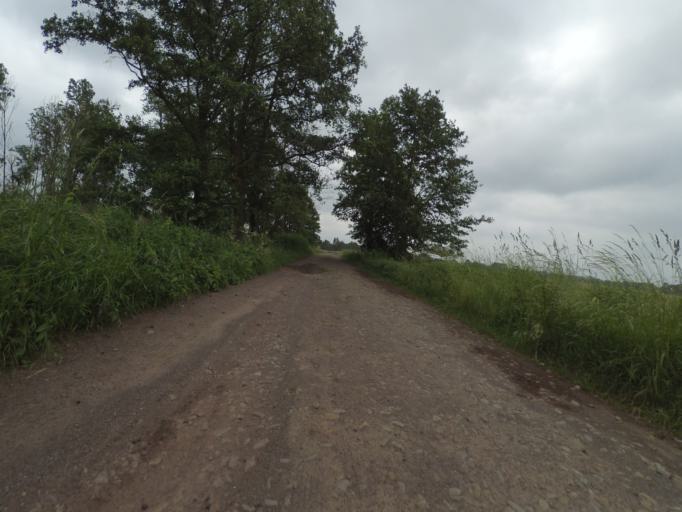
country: DE
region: Mecklenburg-Vorpommern
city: Neustadt-Glewe
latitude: 53.4135
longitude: 11.5724
